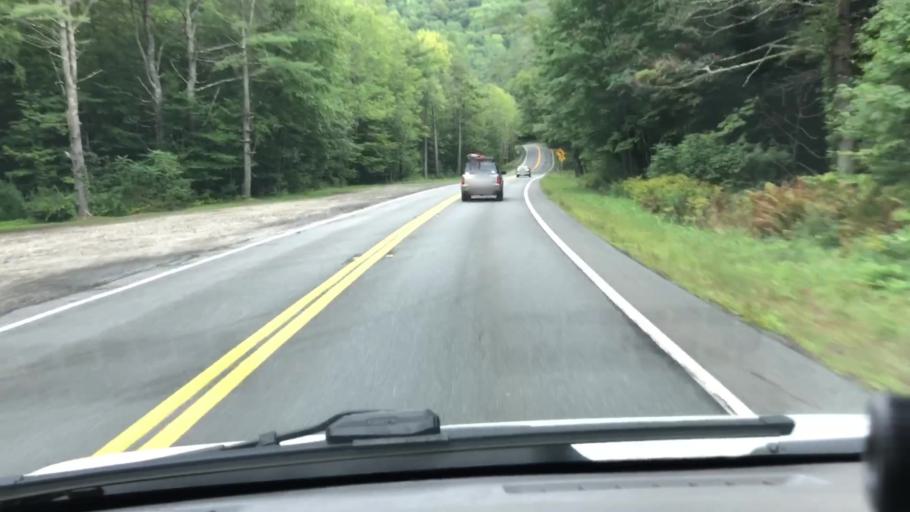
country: US
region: Massachusetts
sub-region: Franklin County
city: Charlemont
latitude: 42.6358
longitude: -72.9350
